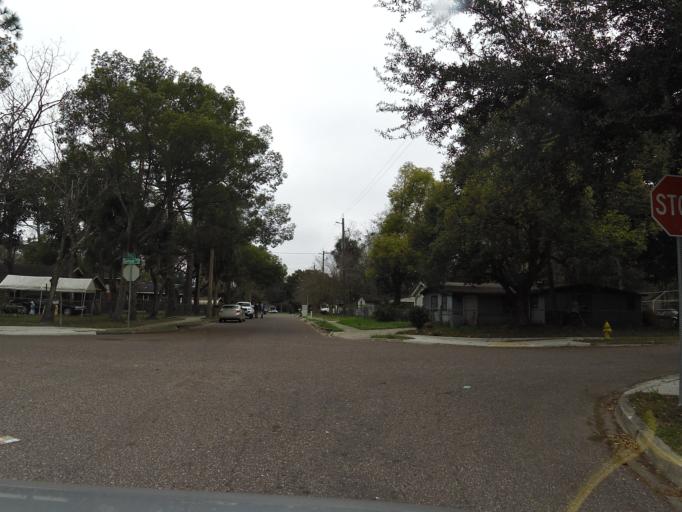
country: US
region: Florida
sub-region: Duval County
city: Jacksonville
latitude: 30.3758
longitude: -81.6957
